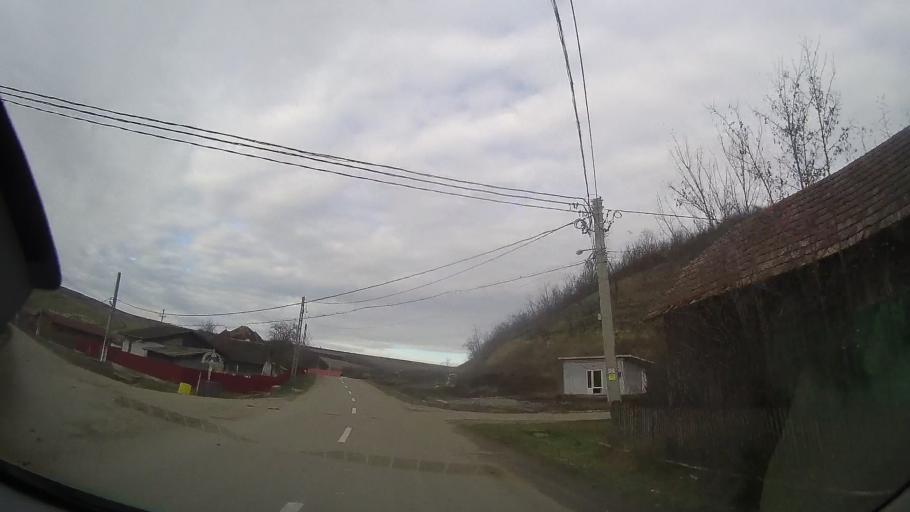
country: RO
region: Bistrita-Nasaud
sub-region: Comuna Silvasu de Campie
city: Silvasu de Campie
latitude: 46.7846
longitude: 24.2876
